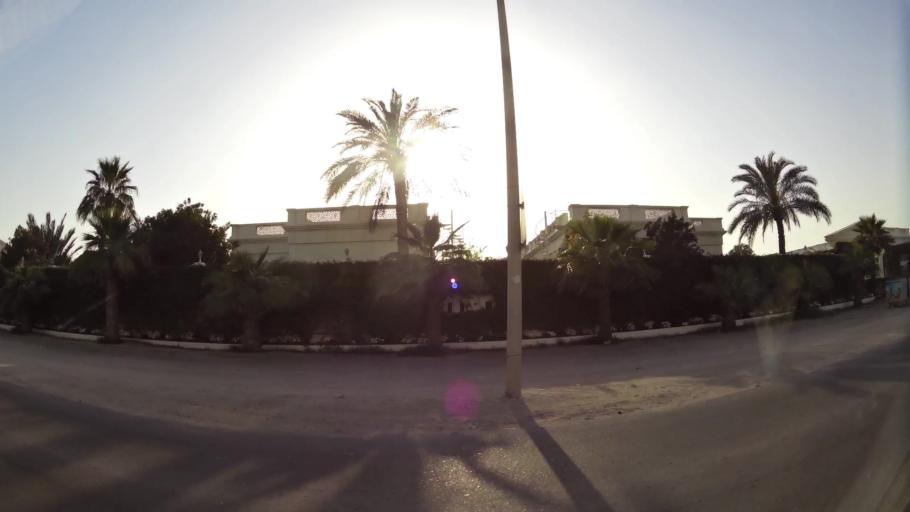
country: BH
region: Manama
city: Jidd Hafs
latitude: 26.2051
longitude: 50.4832
